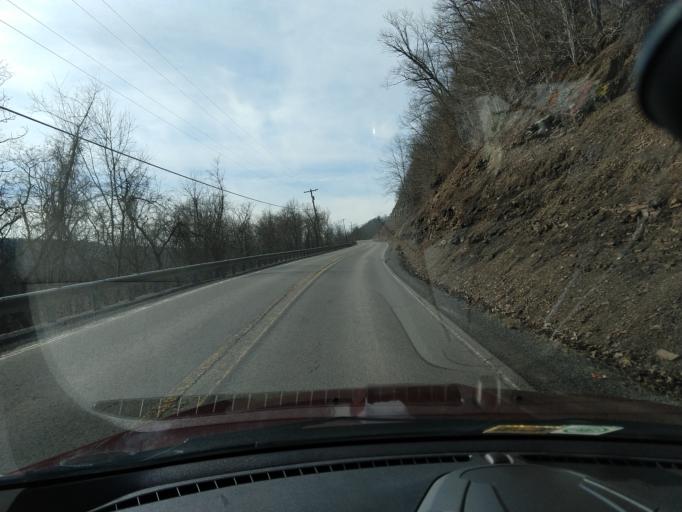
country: US
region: West Virginia
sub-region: Pocahontas County
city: Marlinton
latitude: 38.2176
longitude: -80.1016
